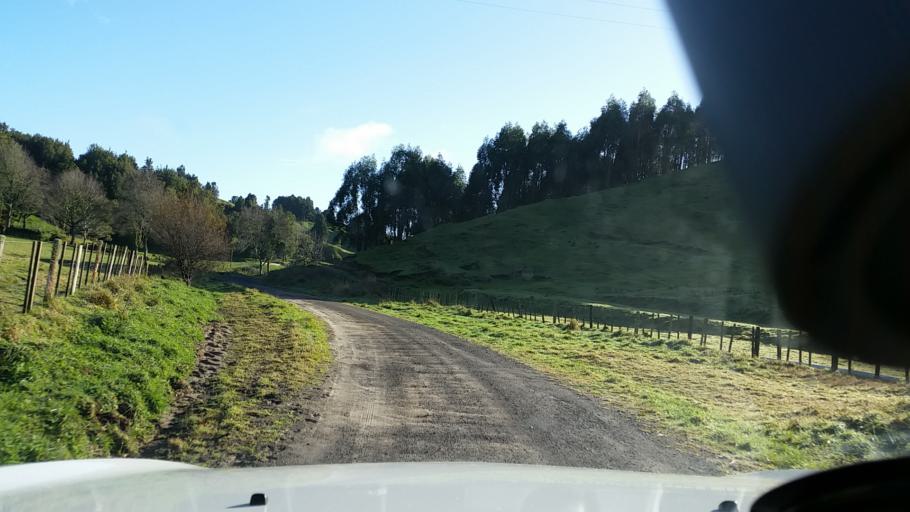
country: NZ
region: Bay of Plenty
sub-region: Kawerau District
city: Kawerau
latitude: -38.0164
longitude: 176.5978
